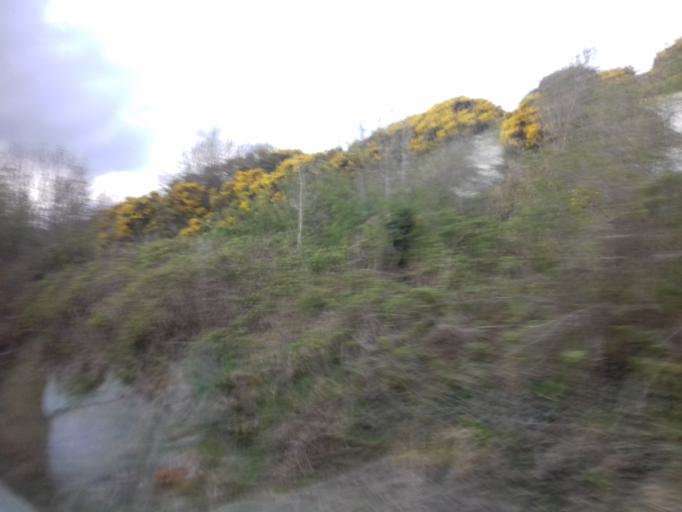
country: IE
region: Leinster
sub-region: An Iarmhi
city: Rathwire
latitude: 53.4880
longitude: -7.1222
